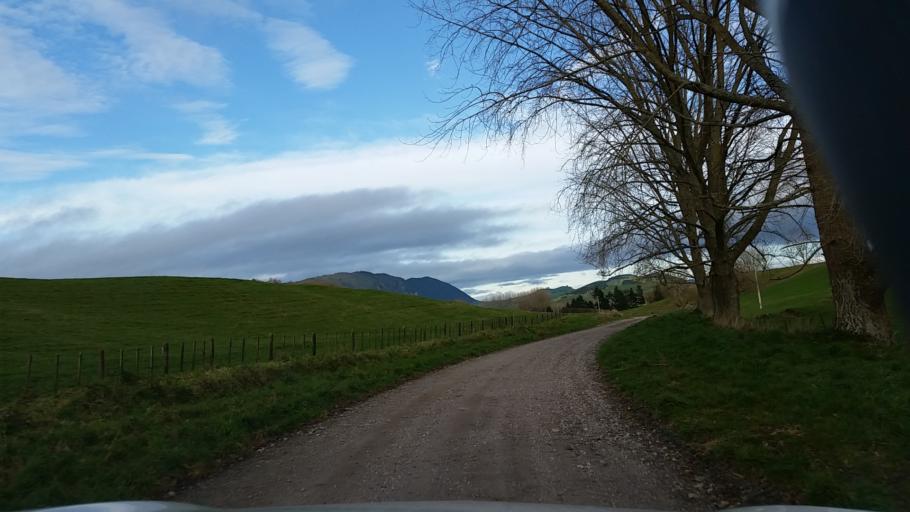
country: NZ
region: Bay of Plenty
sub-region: Rotorua District
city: Rotorua
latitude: -38.3166
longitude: 176.3016
